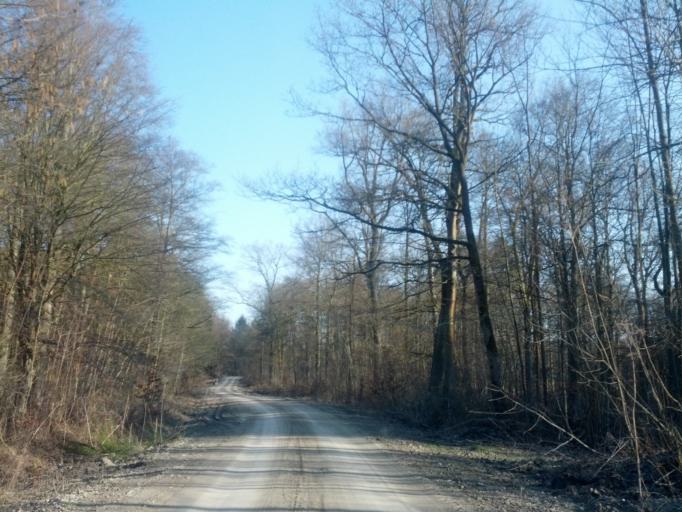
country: DE
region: Thuringia
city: Ebenshausen
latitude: 51.0825
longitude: 10.3048
